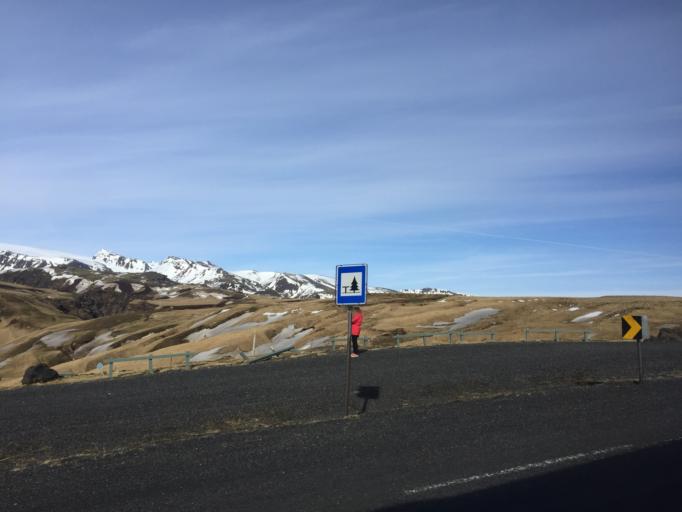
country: IS
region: South
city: Vestmannaeyjar
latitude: 63.4541
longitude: -19.0563
